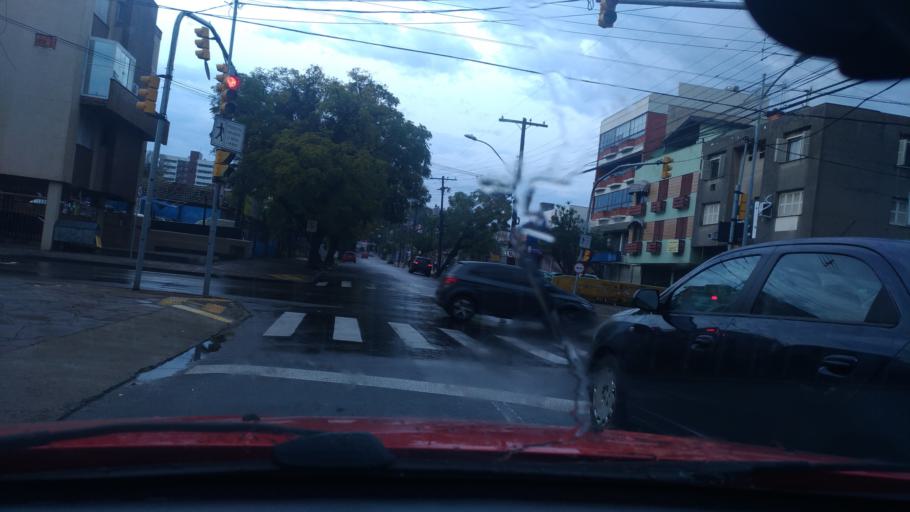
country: BR
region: Rio Grande do Sul
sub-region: Porto Alegre
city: Porto Alegre
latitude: -30.0133
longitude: -51.1649
